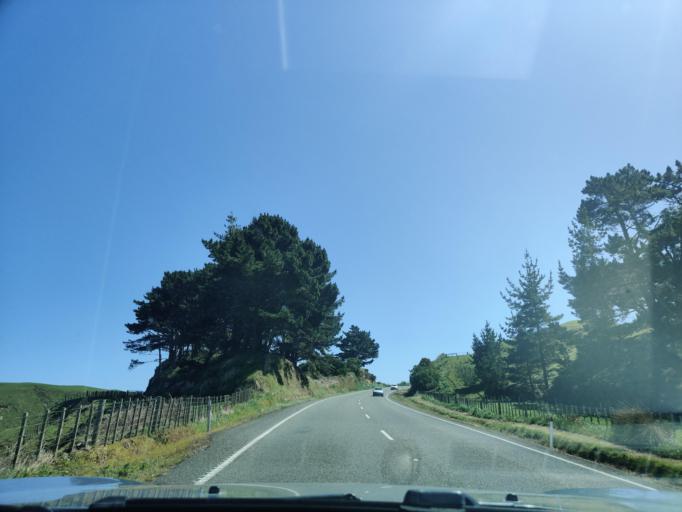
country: NZ
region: Taranaki
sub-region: South Taranaki District
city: Patea
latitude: -39.7553
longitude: 174.5398
